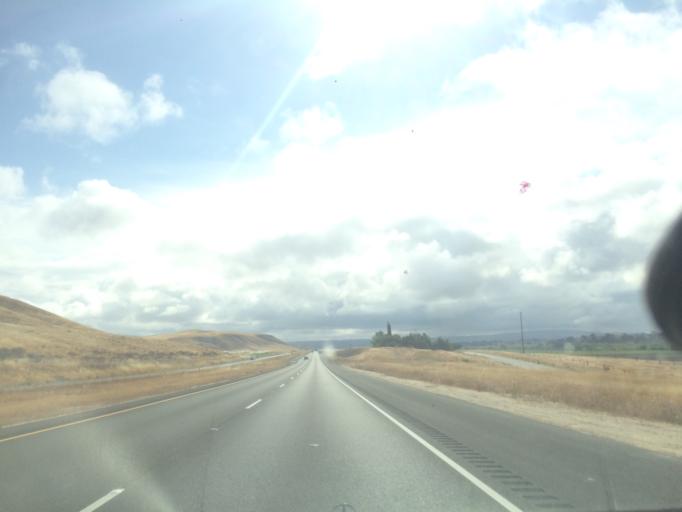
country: US
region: California
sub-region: San Luis Obispo County
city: Shandon
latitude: 35.6595
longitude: -120.4696
